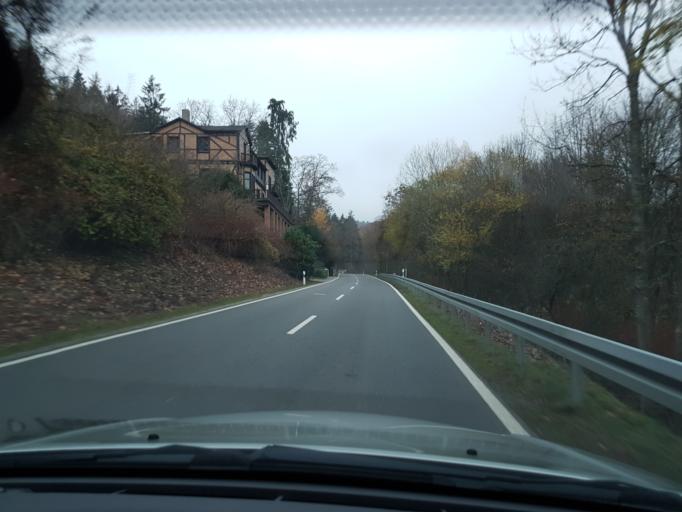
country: DE
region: Hesse
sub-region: Regierungsbezirk Darmstadt
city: Kiedrich
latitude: 50.0533
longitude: 8.0718
